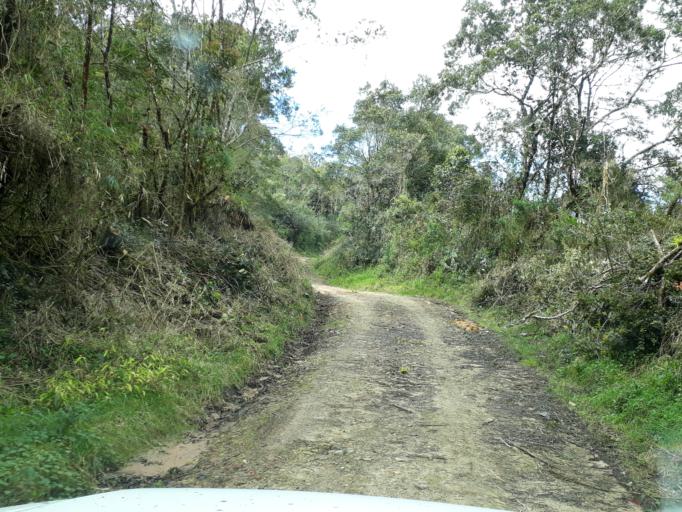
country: CO
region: Cundinamarca
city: Junin
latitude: 4.7858
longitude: -73.7755
